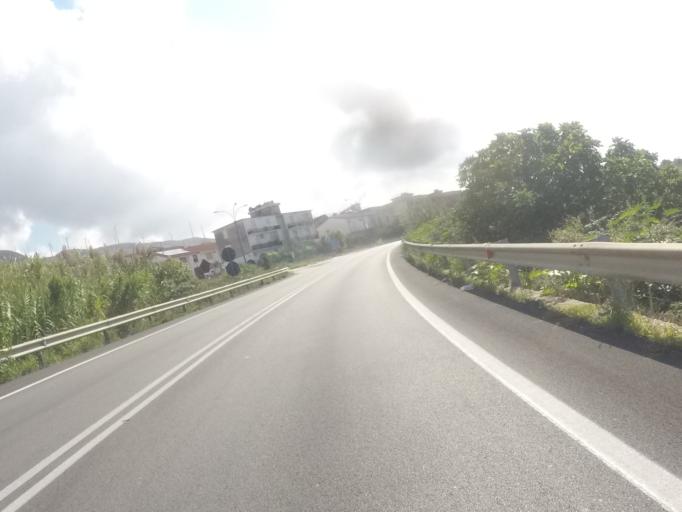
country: IT
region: Sicily
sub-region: Agrigento
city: Siculiana
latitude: 37.3336
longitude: 13.4282
